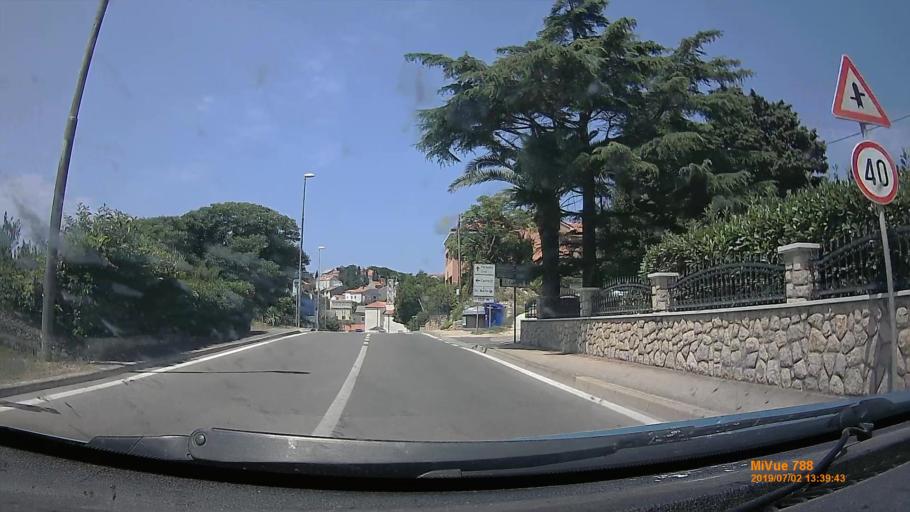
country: HR
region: Primorsko-Goranska
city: Mali Losinj
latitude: 44.5281
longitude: 14.4773
